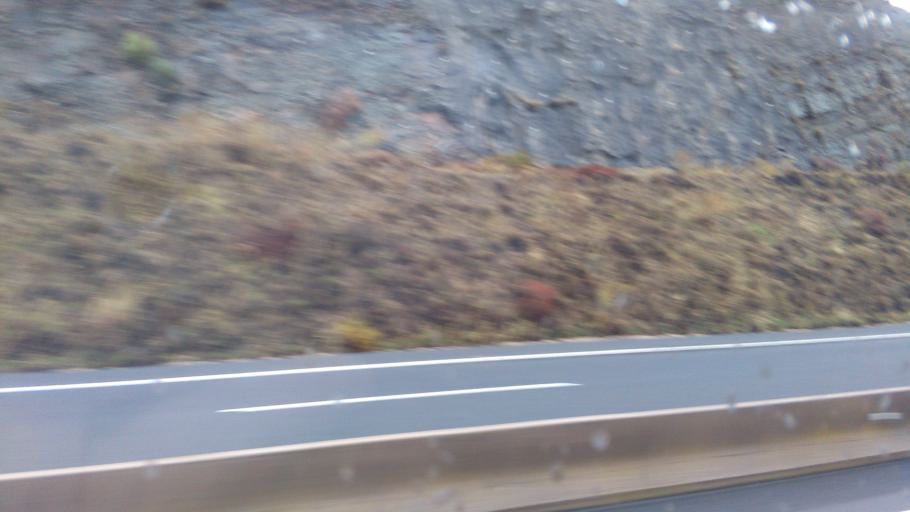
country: ES
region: Extremadura
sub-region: Provincia de Caceres
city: Casas de Miravete
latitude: 39.7559
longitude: -5.7305
